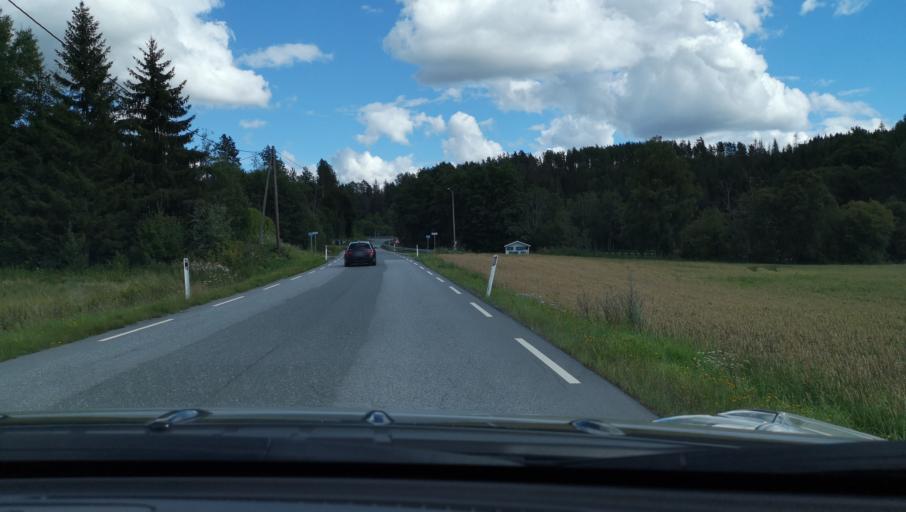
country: NO
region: Ostfold
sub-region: Hobol
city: Elvestad
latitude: 59.6413
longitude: 10.9713
